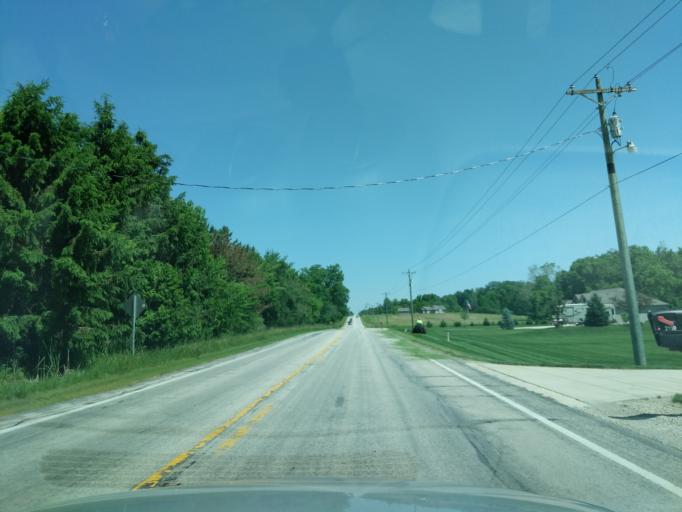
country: US
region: Indiana
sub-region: Whitley County
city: Columbia City
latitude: 41.1942
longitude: -85.4916
